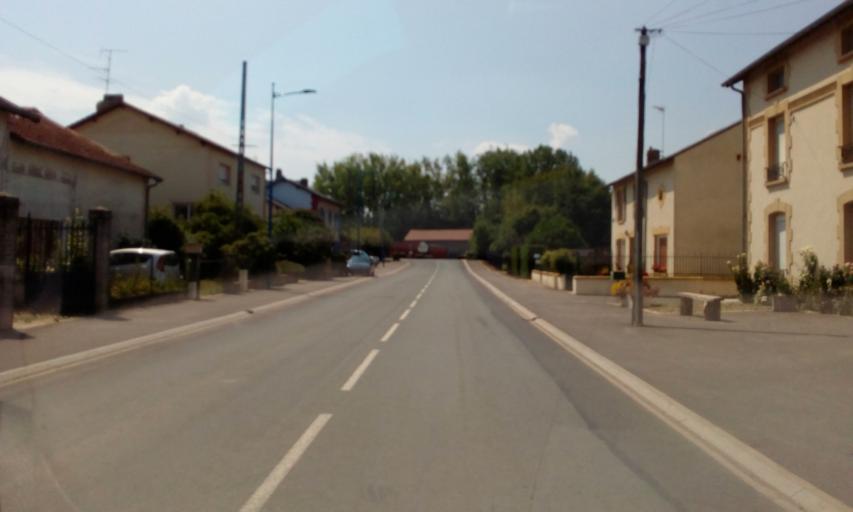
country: FR
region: Lorraine
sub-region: Departement de la Meuse
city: Etain
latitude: 49.0956
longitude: 5.6261
